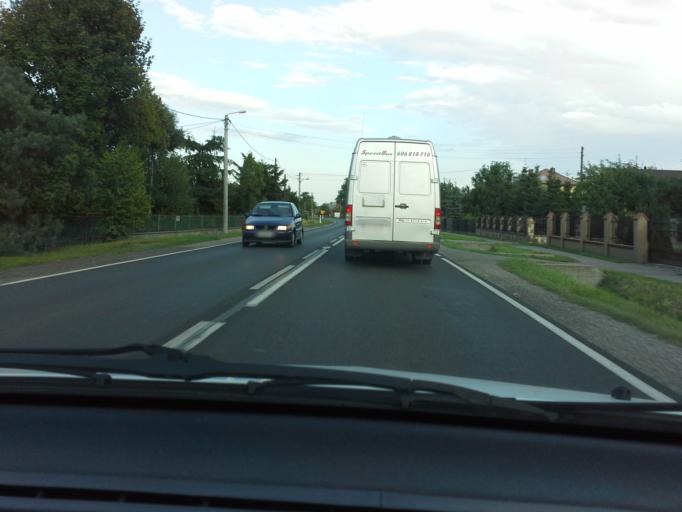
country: PL
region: Lesser Poland Voivodeship
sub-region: Powiat krakowski
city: Wola Filipowska
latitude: 50.1313
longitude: 19.5942
